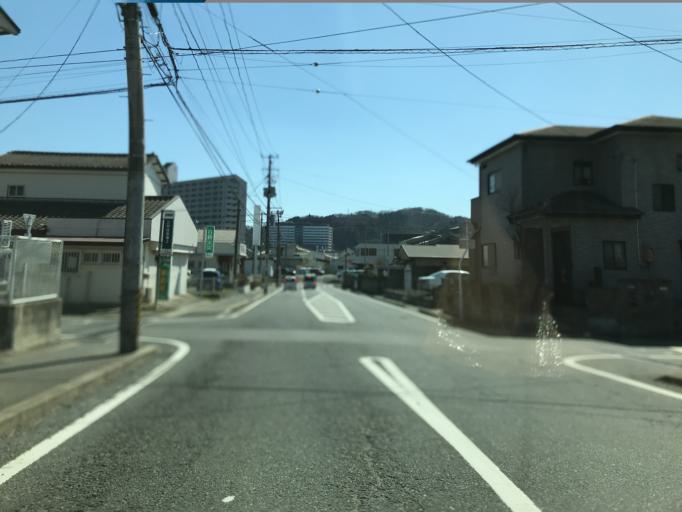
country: JP
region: Fukushima
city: Iwaki
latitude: 37.0471
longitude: 140.8620
